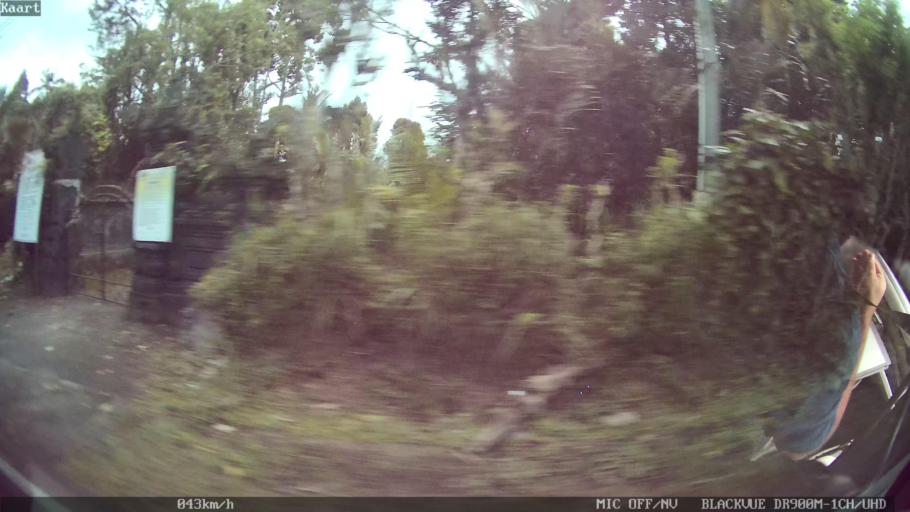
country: ID
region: Bali
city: Banjar Tiga
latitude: -8.3898
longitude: 115.4189
